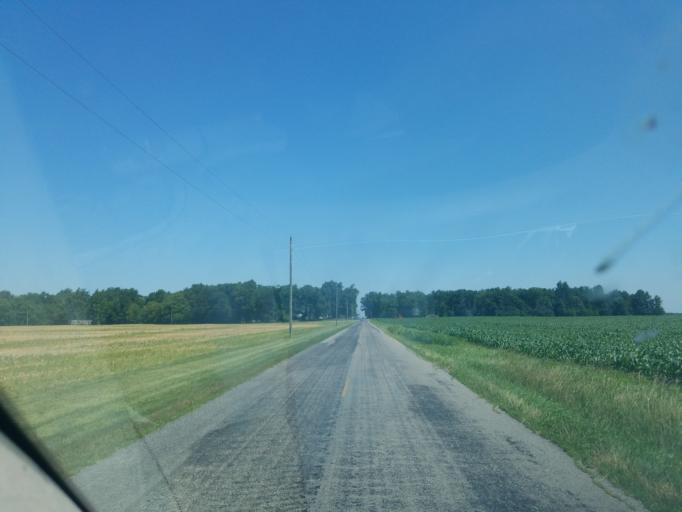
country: US
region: Ohio
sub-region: Mercer County
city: Saint Henry
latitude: 40.4539
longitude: -84.7080
